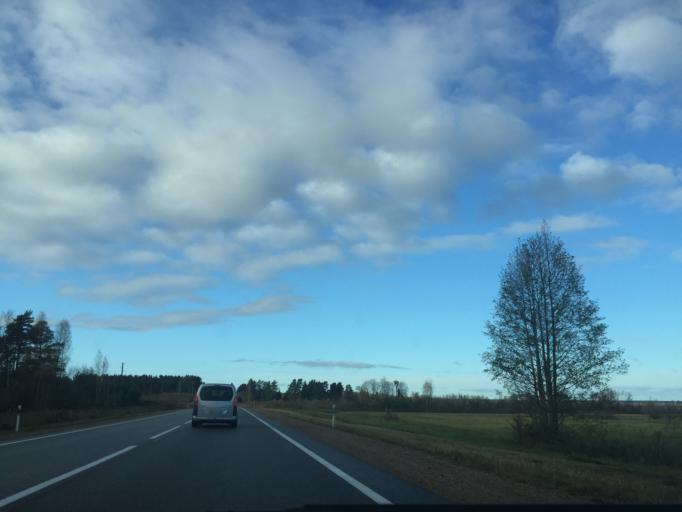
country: LV
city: Tireli
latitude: 56.8910
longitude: 23.6873
